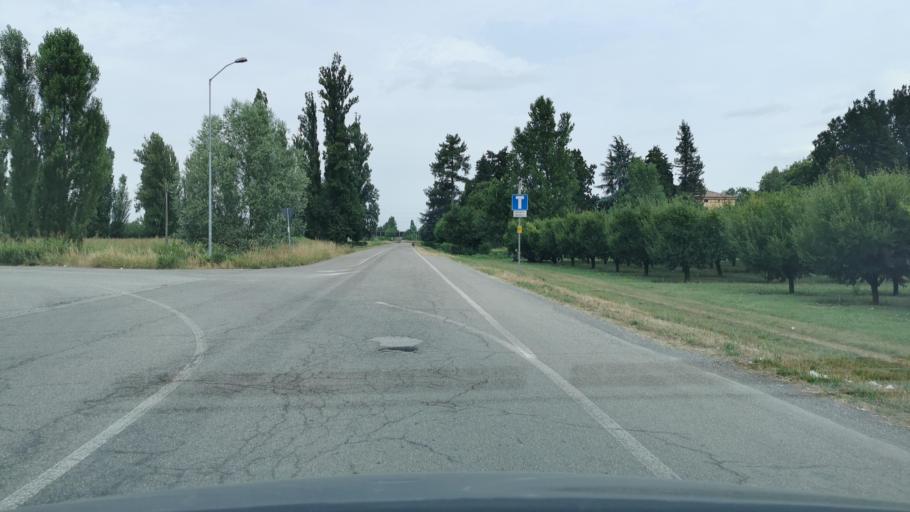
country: IT
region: Emilia-Romagna
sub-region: Provincia di Modena
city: Campogalliano
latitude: 44.6830
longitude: 10.8757
